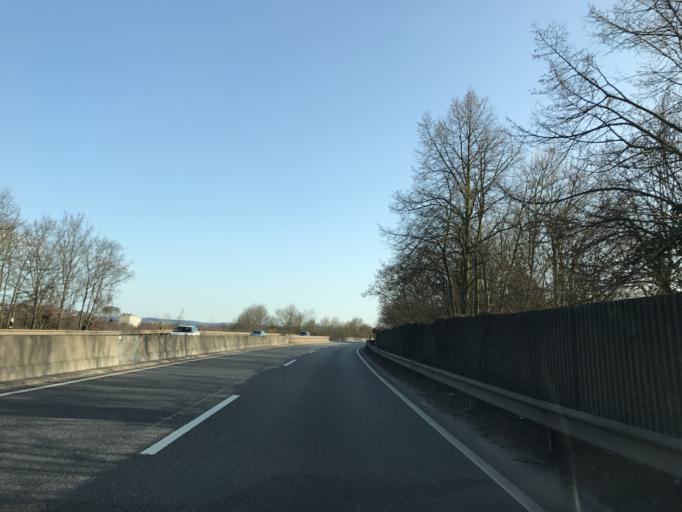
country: DE
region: Rheinland-Pfalz
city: Sankt Sebastian
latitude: 50.4267
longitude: 7.5586
